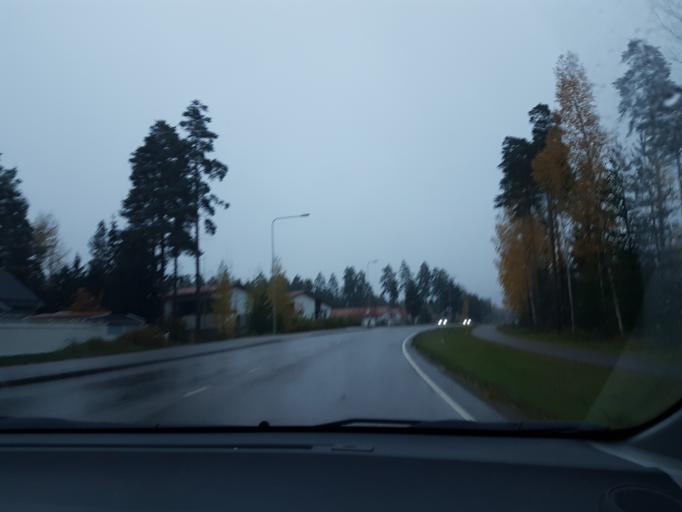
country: FI
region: Uusimaa
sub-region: Helsinki
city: Tuusula
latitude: 60.4013
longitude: 24.9853
